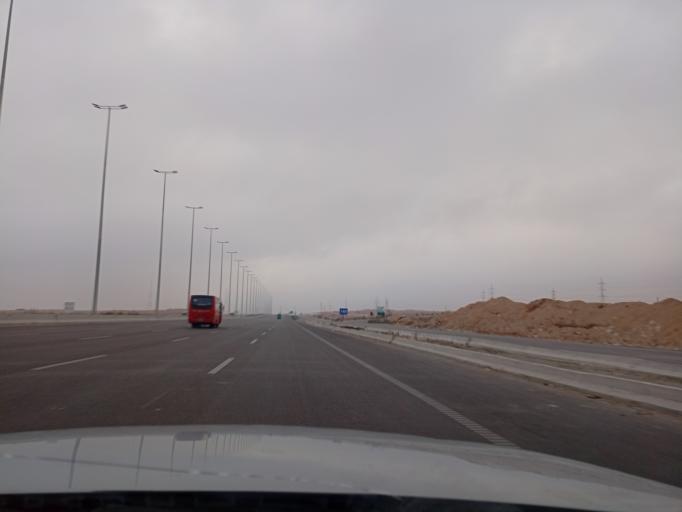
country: EG
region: Muhafazat al Qalyubiyah
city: Al Khankah
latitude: 30.0856
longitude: 31.5224
